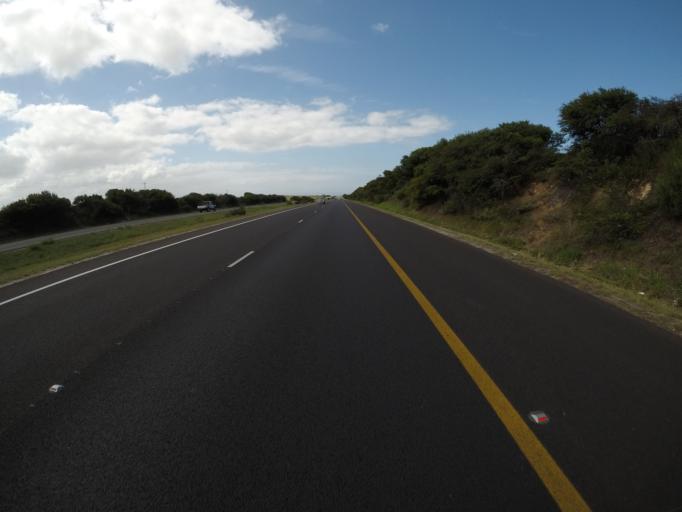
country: ZA
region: Western Cape
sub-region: Eden District Municipality
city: Mossel Bay
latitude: -34.1683
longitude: 22.0804
